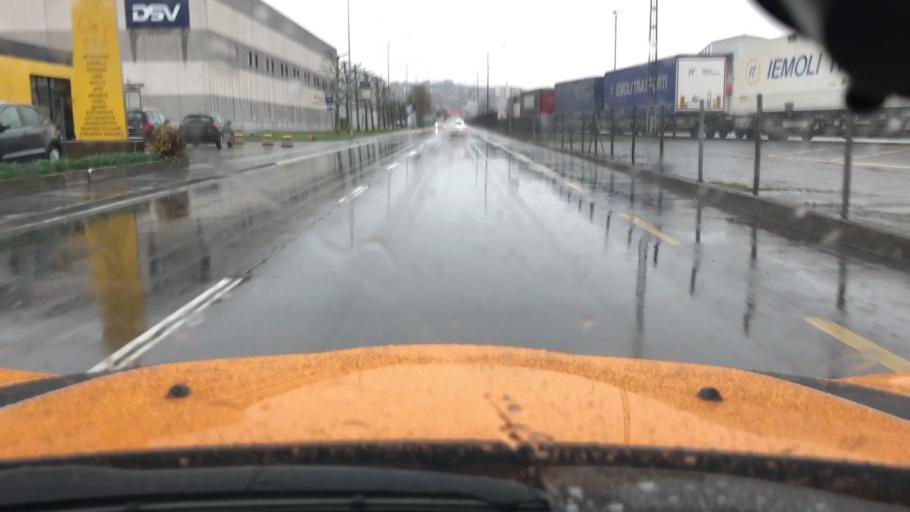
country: CH
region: Ticino
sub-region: Mendrisio District
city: Balerna
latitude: 45.8358
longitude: 9.0137
